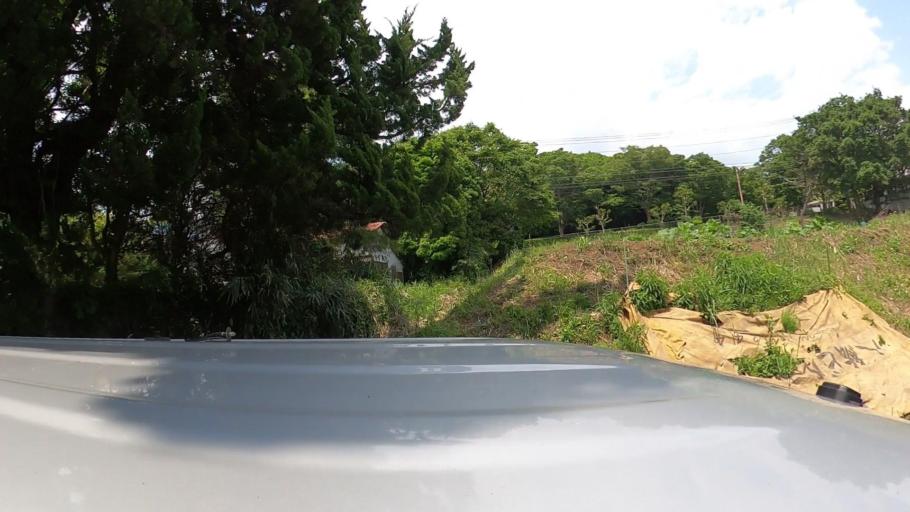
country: JP
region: Kanagawa
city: Fujisawa
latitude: 35.3841
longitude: 139.4256
